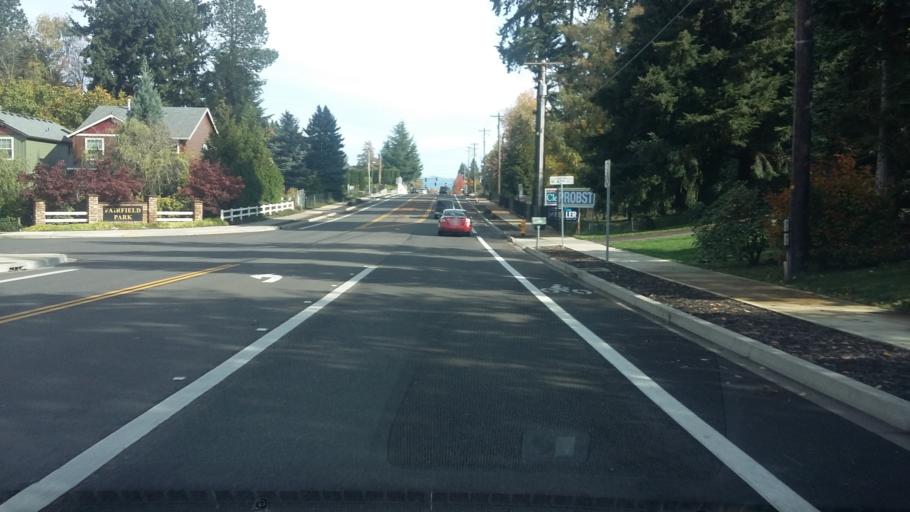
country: US
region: Washington
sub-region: Clark County
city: Barberton
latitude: 45.6859
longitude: -122.6292
